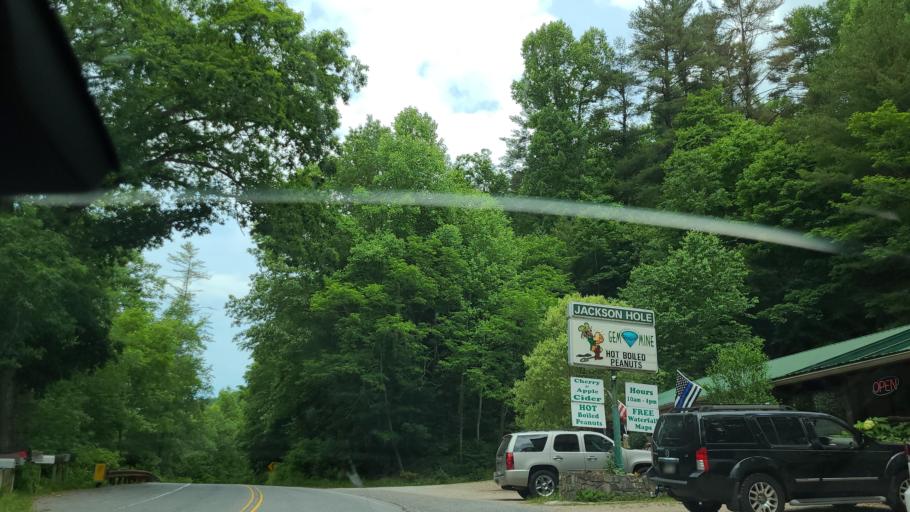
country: US
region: North Carolina
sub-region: Macon County
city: Franklin
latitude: 35.1132
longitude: -83.2648
